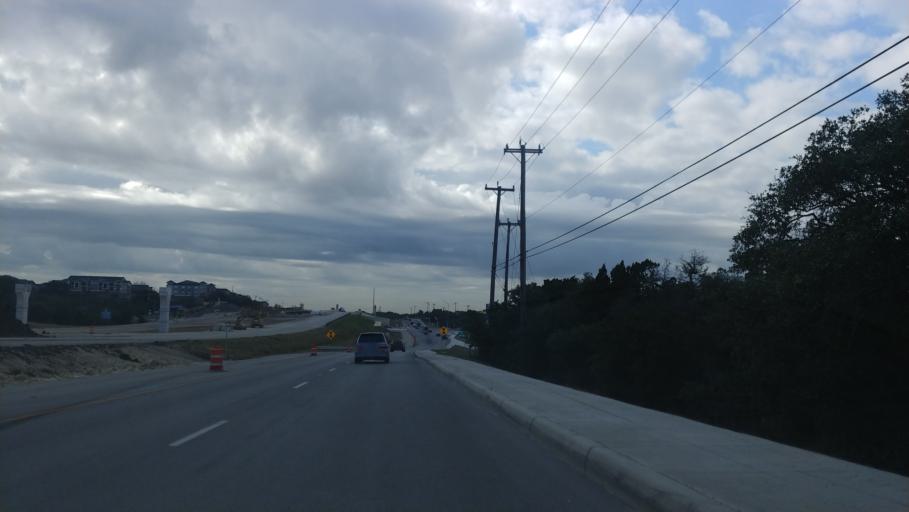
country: US
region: Texas
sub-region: Bexar County
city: Leon Valley
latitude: 29.4694
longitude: -98.7117
